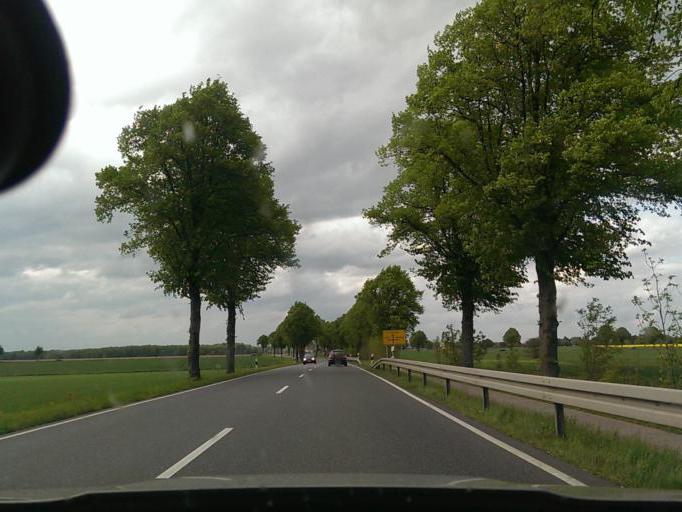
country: DE
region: Lower Saxony
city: Nordstemmen
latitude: 52.2054
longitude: 9.7473
